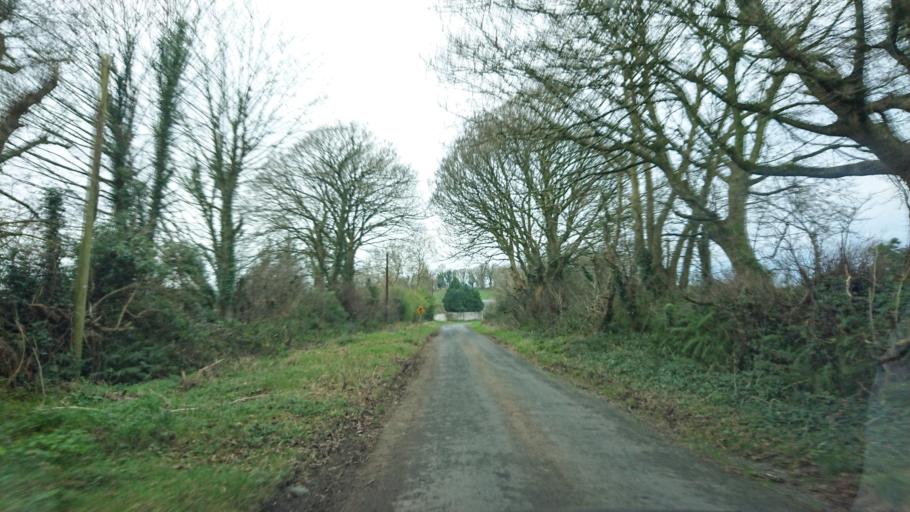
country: IE
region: Leinster
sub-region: Kilkenny
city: Mooncoin
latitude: 52.2293
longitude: -7.2543
